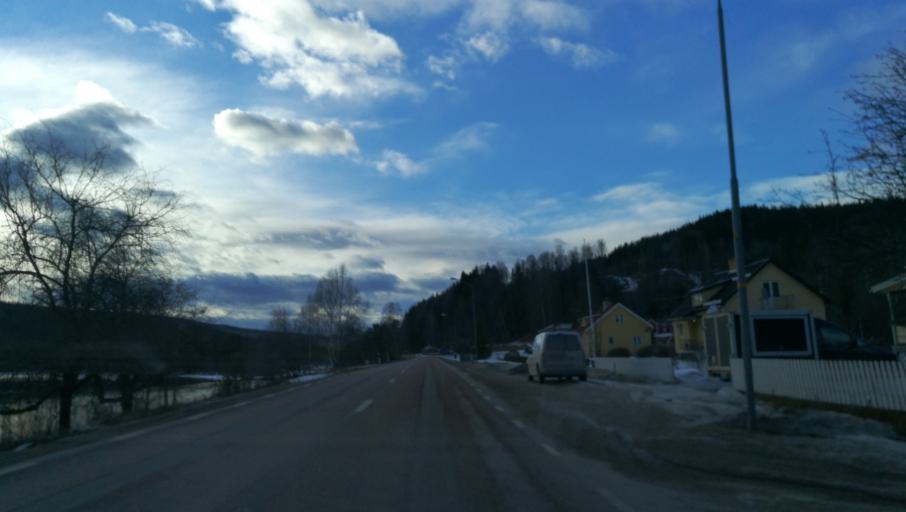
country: SE
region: Vaermland
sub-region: Torsby Kommun
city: Torsby
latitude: 60.7390
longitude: 12.8522
